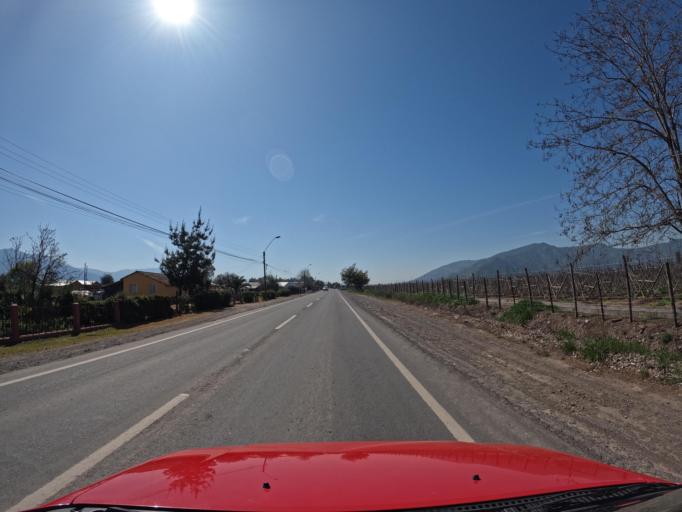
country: CL
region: Maule
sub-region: Provincia de Curico
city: Rauco
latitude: -35.0370
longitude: -71.4491
